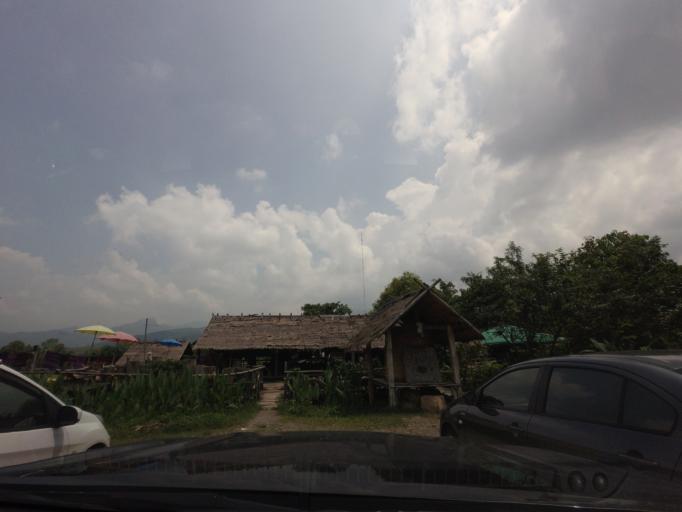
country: TH
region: Nan
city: Pua
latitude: 19.1456
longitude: 100.9405
